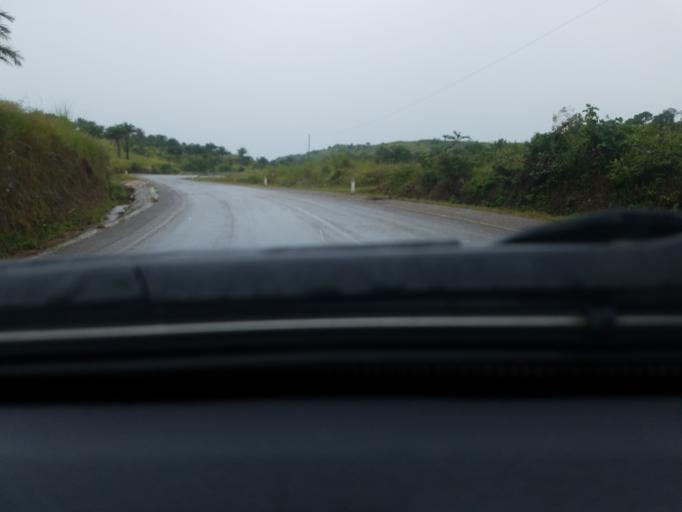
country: TZ
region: Kigoma
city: Mwandiga
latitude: -4.6711
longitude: 29.7248
